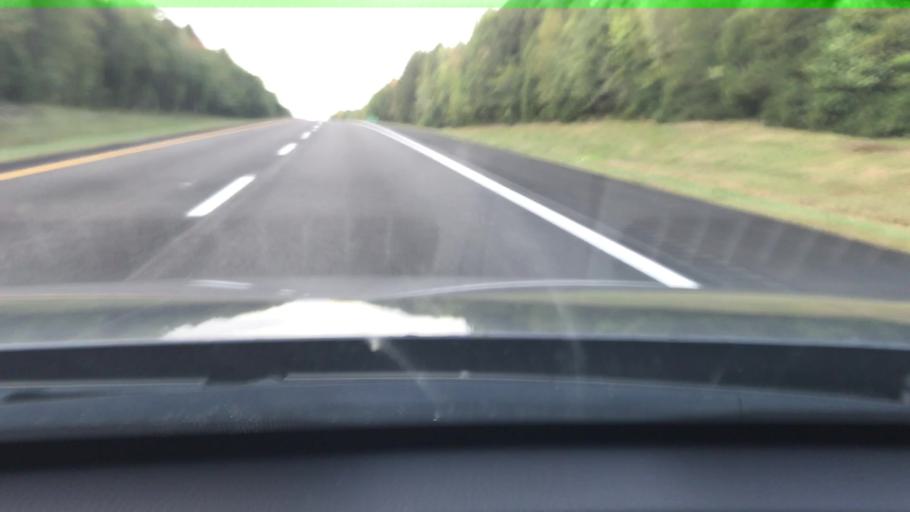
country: US
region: Maine
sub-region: Sagadahoc County
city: Richmond
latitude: 44.0913
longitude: -69.8750
